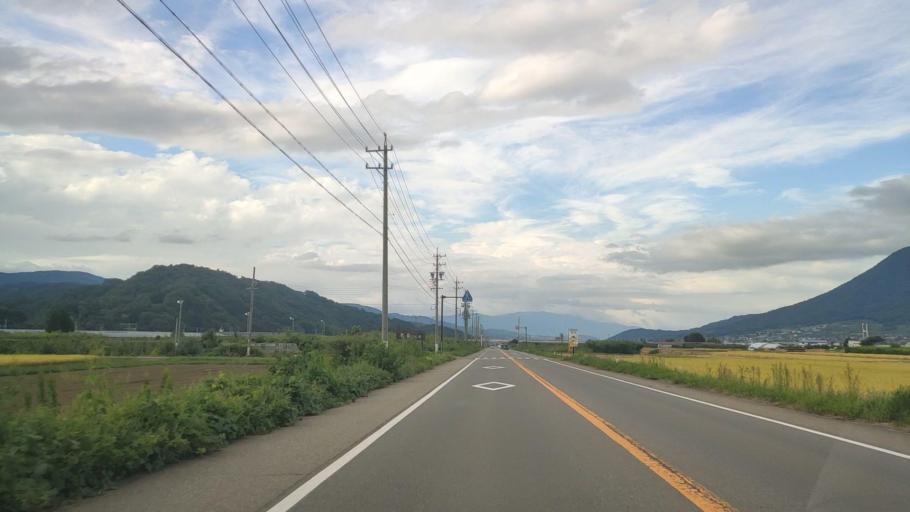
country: JP
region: Nagano
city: Nakano
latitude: 36.7738
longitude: 138.3506
